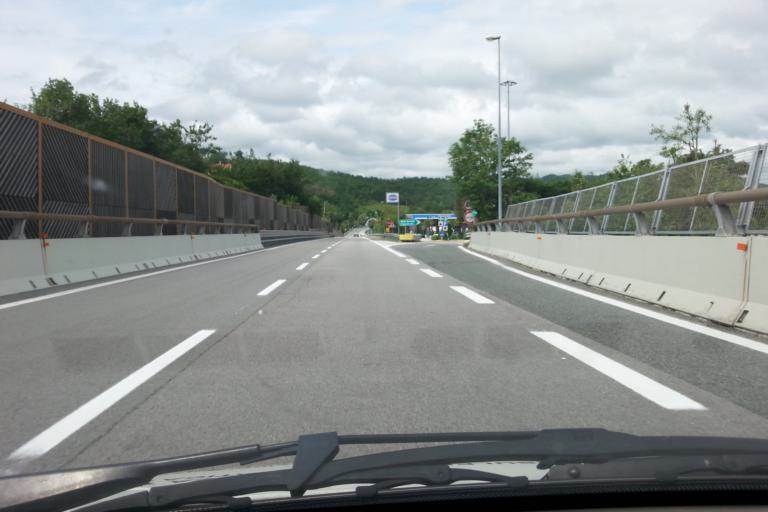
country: IT
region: Liguria
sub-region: Provincia di Savona
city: Carcare
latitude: 44.3468
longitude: 8.3036
